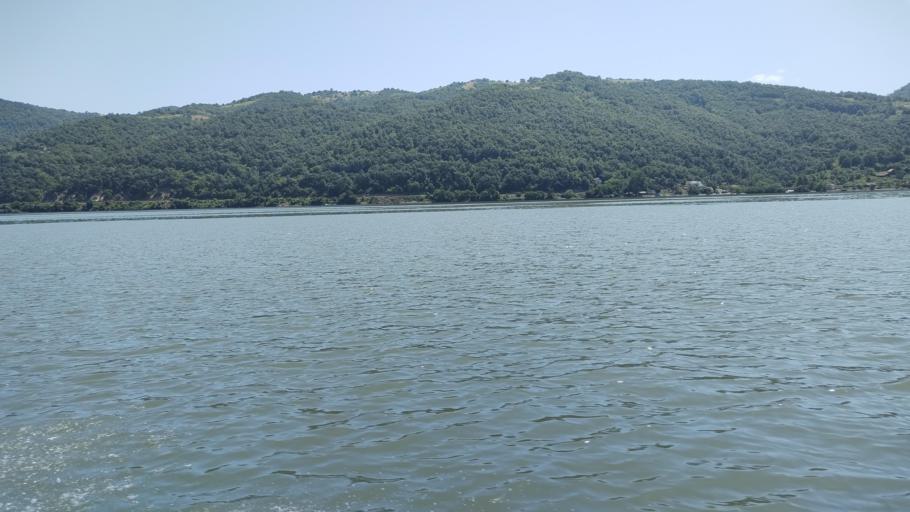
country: RO
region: Mehedinti
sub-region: Comuna Svinita
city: Svinita
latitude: 44.5090
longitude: 22.1947
